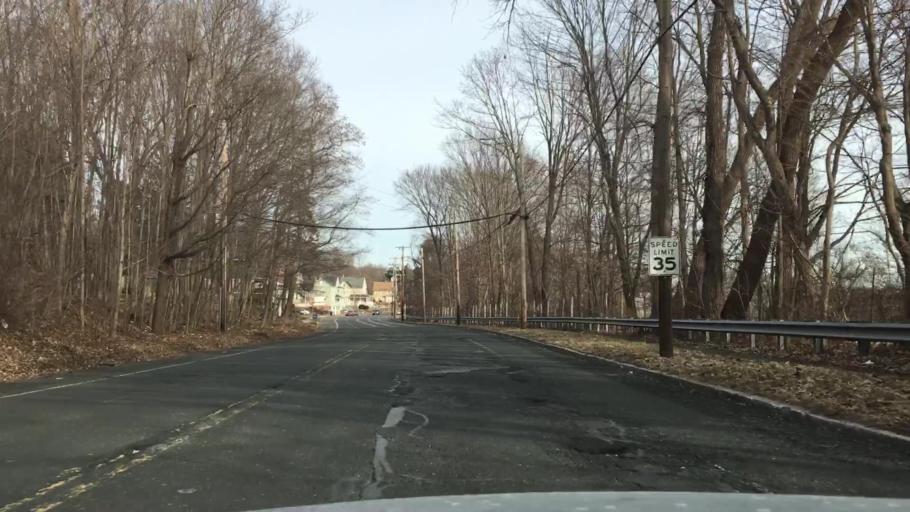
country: US
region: Massachusetts
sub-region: Hampden County
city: Chicopee
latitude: 42.1706
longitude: -72.6320
